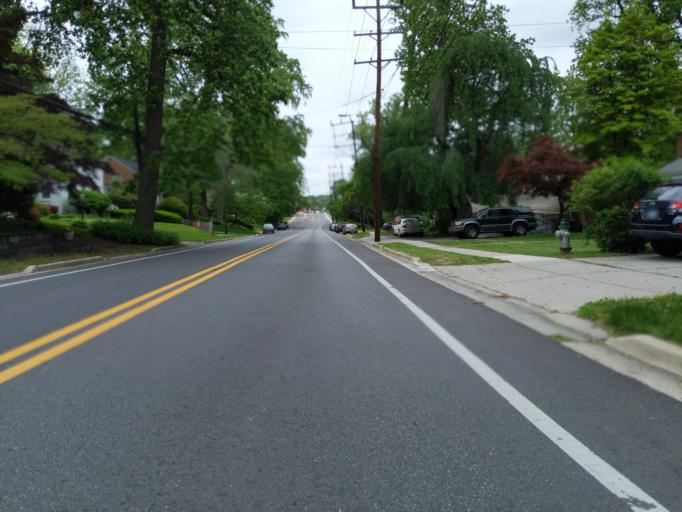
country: US
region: Maryland
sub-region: Montgomery County
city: Forest Glen
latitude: 39.0116
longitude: -77.0505
